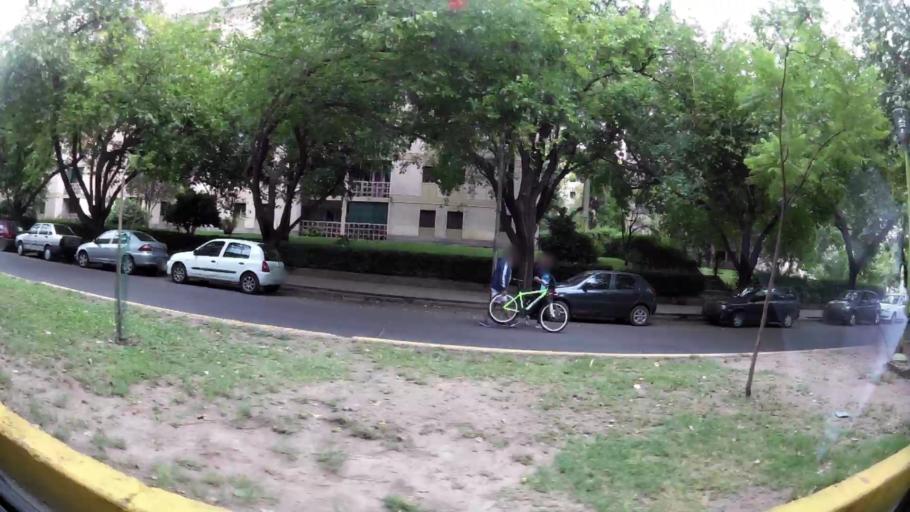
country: AR
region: Mendoza
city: Mendoza
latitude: -32.8741
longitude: -68.8403
